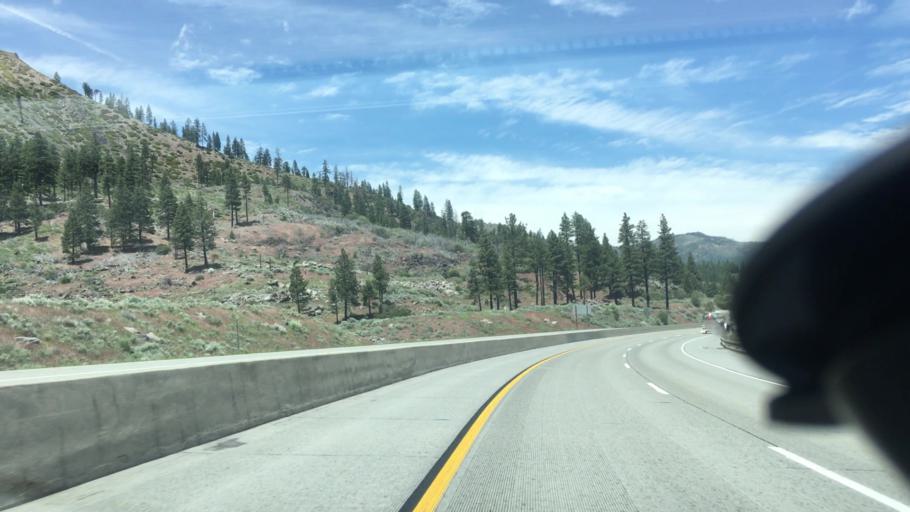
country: US
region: Nevada
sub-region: Washoe County
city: Verdi
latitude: 39.3855
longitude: -120.0247
